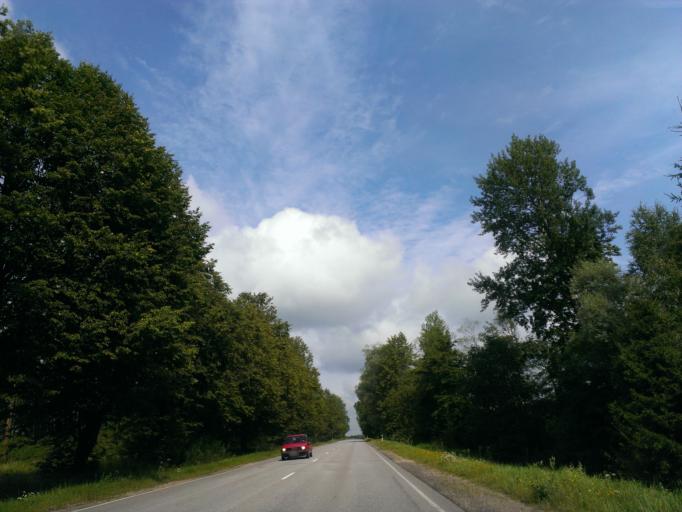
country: LV
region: Amatas Novads
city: Drabesi
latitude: 57.2392
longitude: 25.2903
